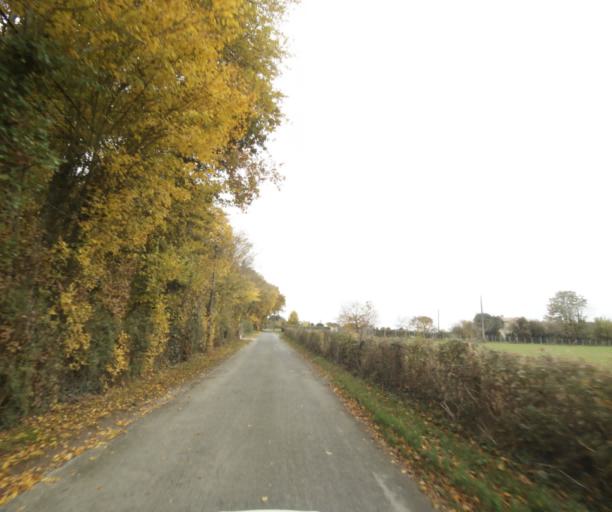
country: FR
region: Poitou-Charentes
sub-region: Departement de la Charente-Maritime
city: Saintes
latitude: 45.7647
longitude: -0.6327
